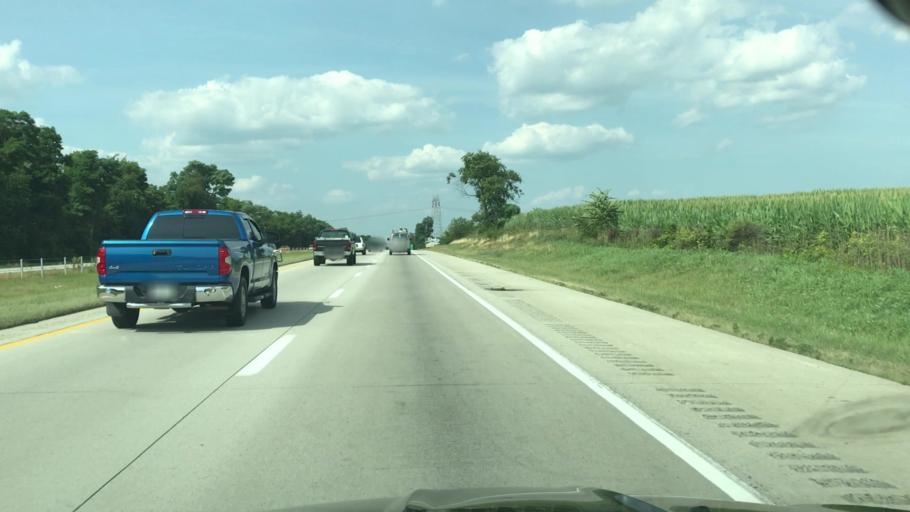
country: US
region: Pennsylvania
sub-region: Franklin County
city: Scotland
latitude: 39.9988
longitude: -77.5531
